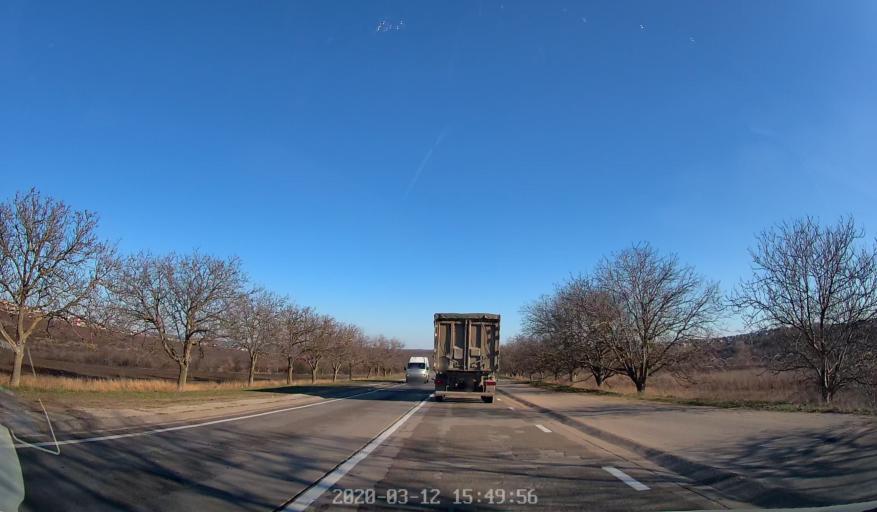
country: MD
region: Chisinau
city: Ciorescu
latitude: 47.0773
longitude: 28.9489
